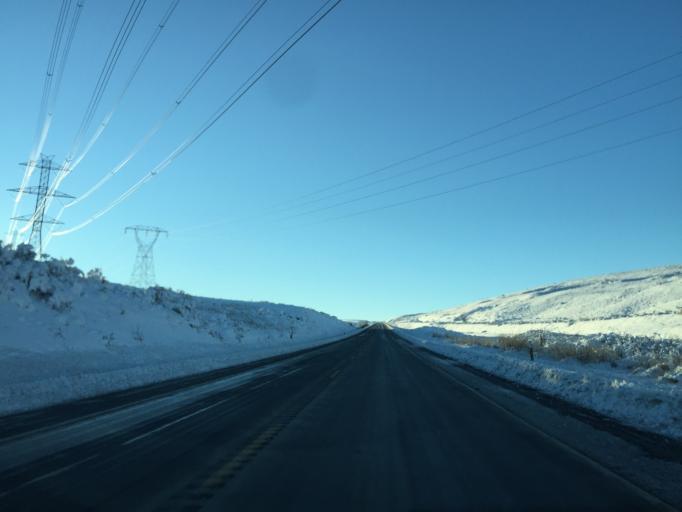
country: US
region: Washington
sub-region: Grant County
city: Soap Lake
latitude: 47.6224
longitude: -119.3927
